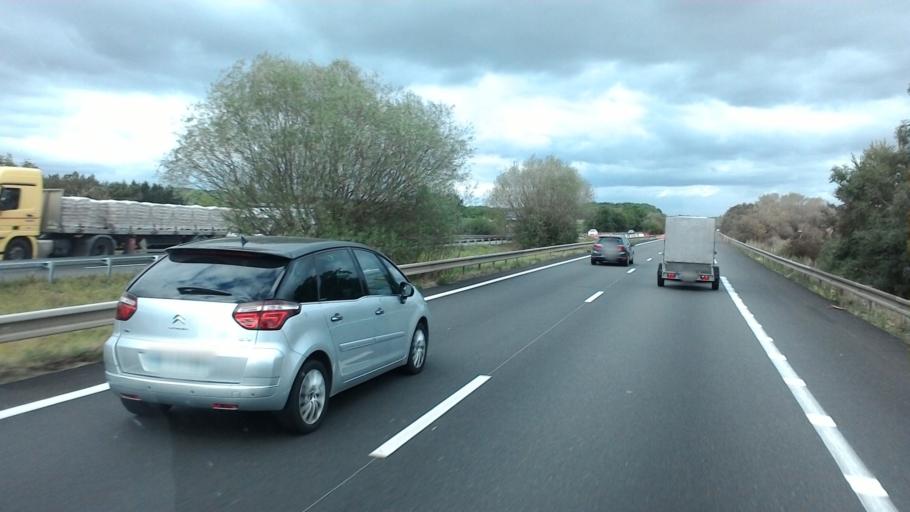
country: FR
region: Lorraine
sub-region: Departement de la Moselle
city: Corny-sur-Moselle
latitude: 49.0024
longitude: 6.1073
